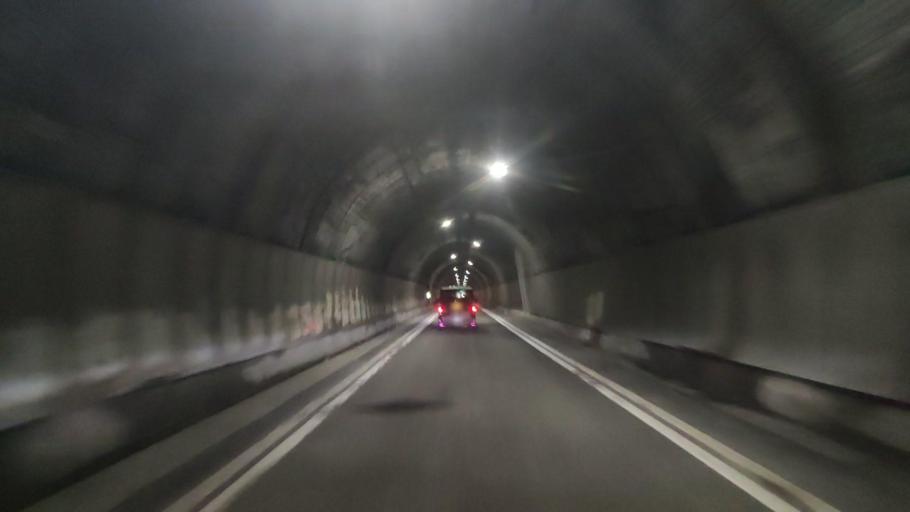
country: JP
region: Fukui
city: Takefu
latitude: 35.8423
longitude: 136.1236
